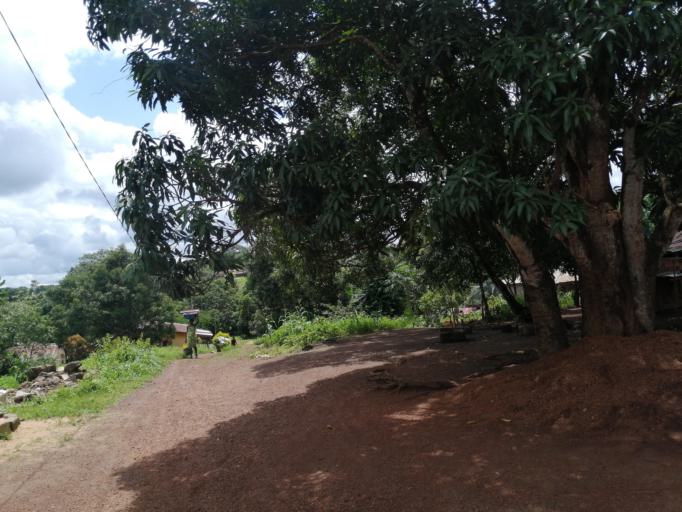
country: SL
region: Northern Province
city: Port Loko
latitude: 8.7702
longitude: -12.7826
